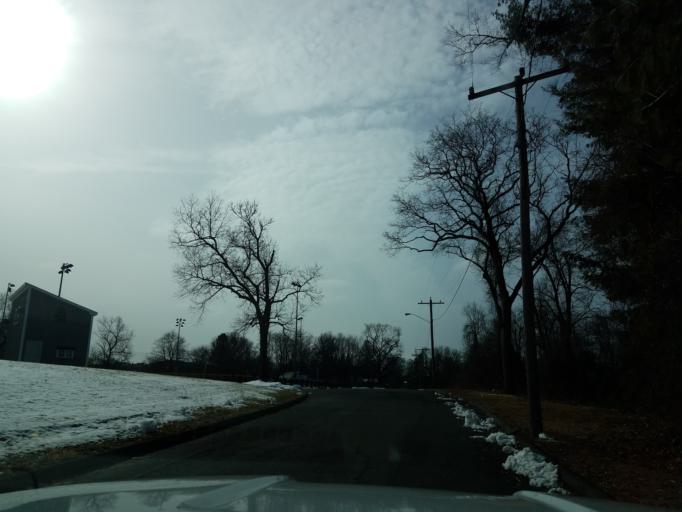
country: US
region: Connecticut
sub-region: Hartford County
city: Weatogue
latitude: 41.8151
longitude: -72.8295
